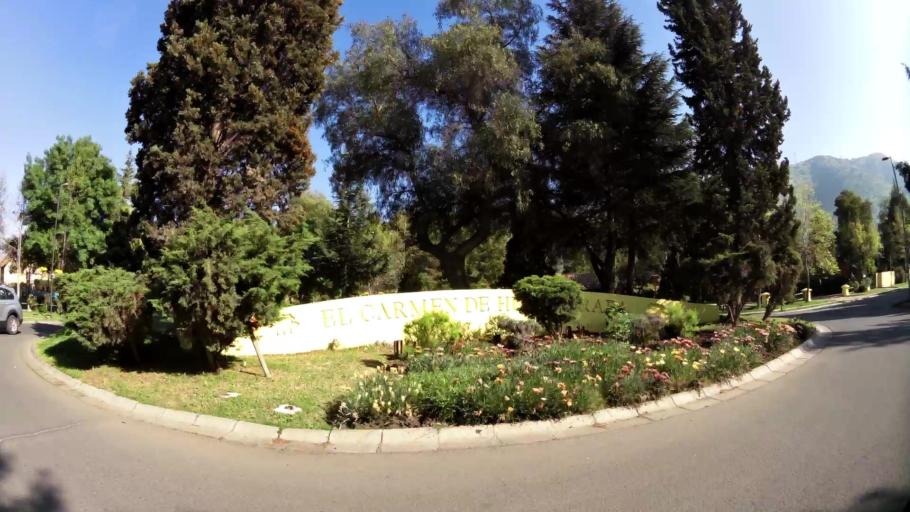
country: CL
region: Santiago Metropolitan
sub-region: Provincia de Chacabuco
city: Chicureo Abajo
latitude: -33.3495
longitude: -70.6788
